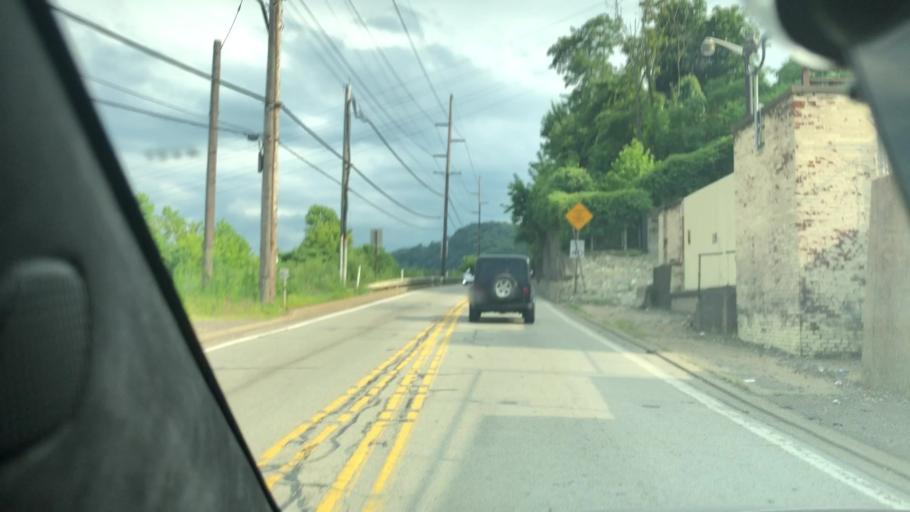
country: US
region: Pennsylvania
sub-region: Allegheny County
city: Mount Oliver
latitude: 40.4099
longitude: -79.9551
